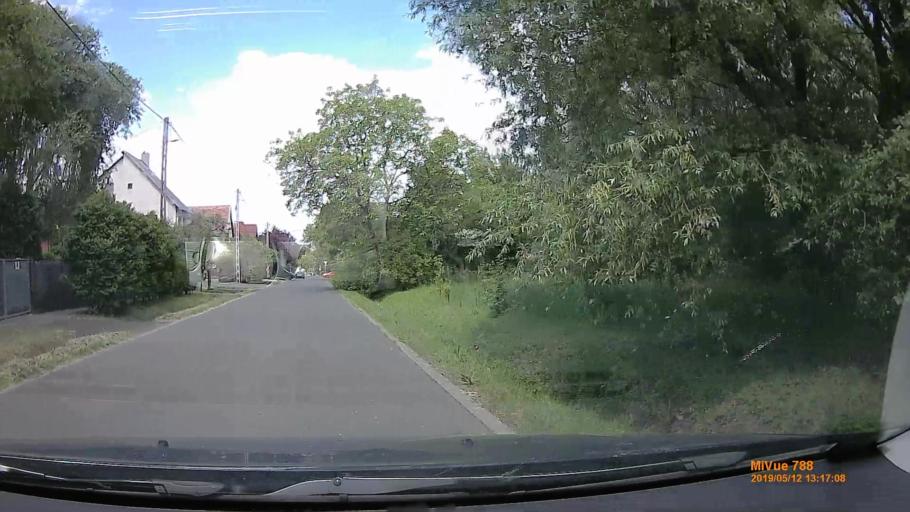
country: HU
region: Budapest
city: Budapest XVII. keruelet
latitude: 47.4808
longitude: 19.2881
